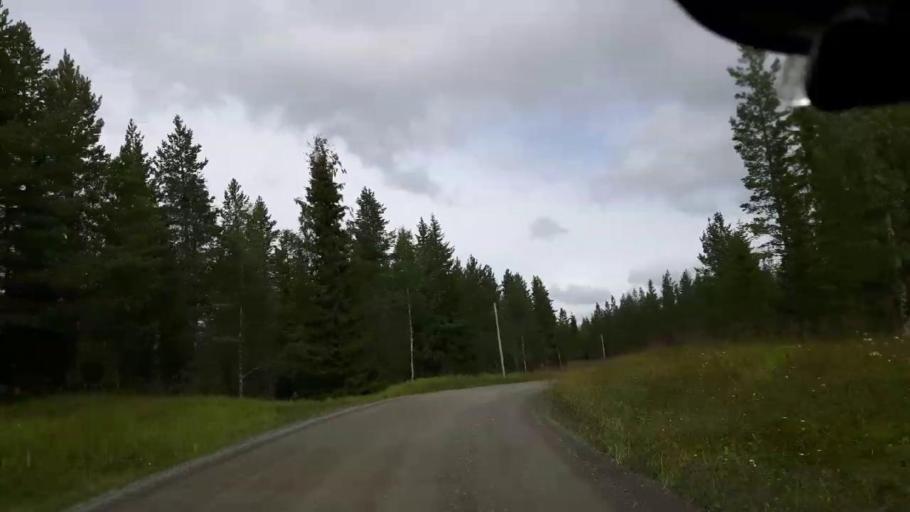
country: SE
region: Jaemtland
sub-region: Krokoms Kommun
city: Valla
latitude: 63.4140
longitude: 14.0852
